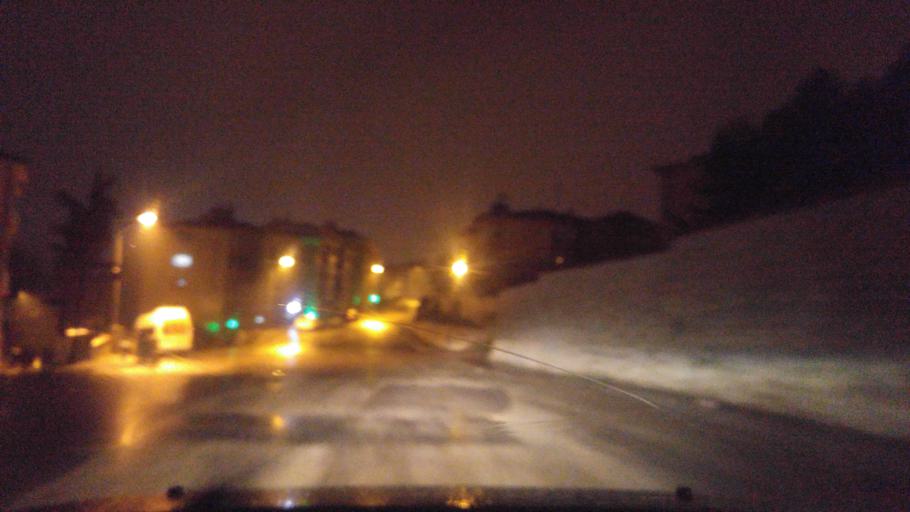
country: TR
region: Karabuk
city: Safranbolu
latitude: 41.2596
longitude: 32.6809
